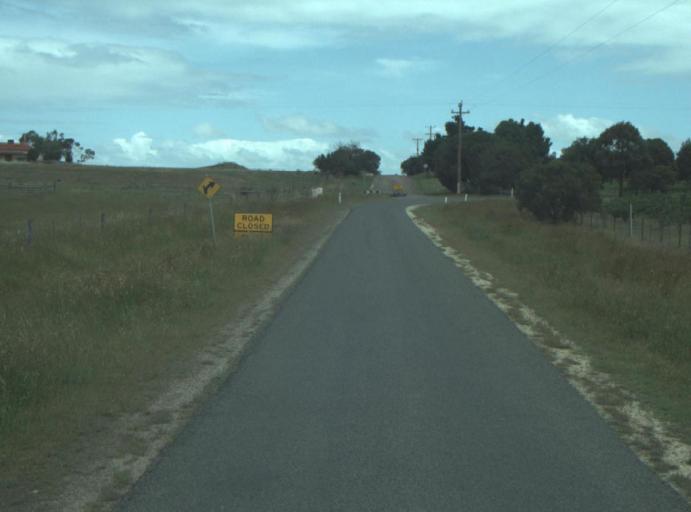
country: AU
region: Victoria
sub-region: Greater Geelong
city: Breakwater
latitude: -38.2227
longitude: 144.3751
